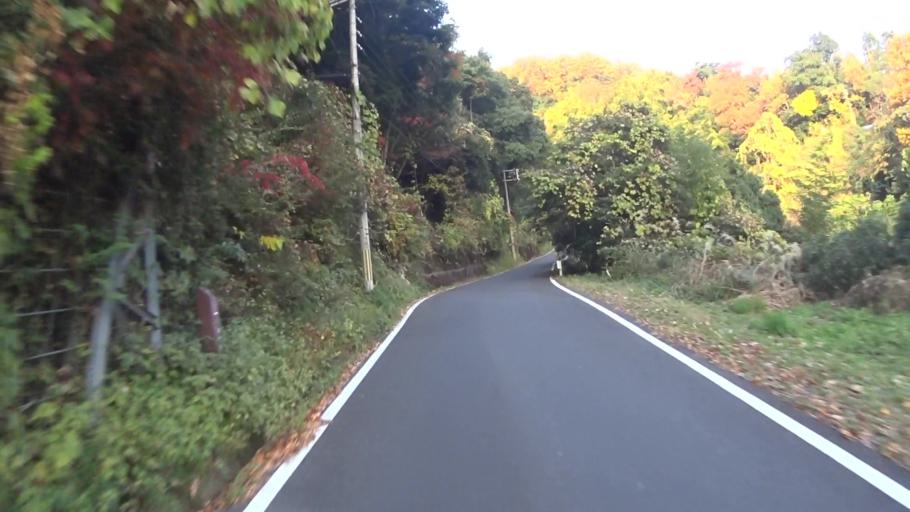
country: JP
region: Kyoto
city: Maizuru
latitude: 35.4959
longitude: 135.4655
